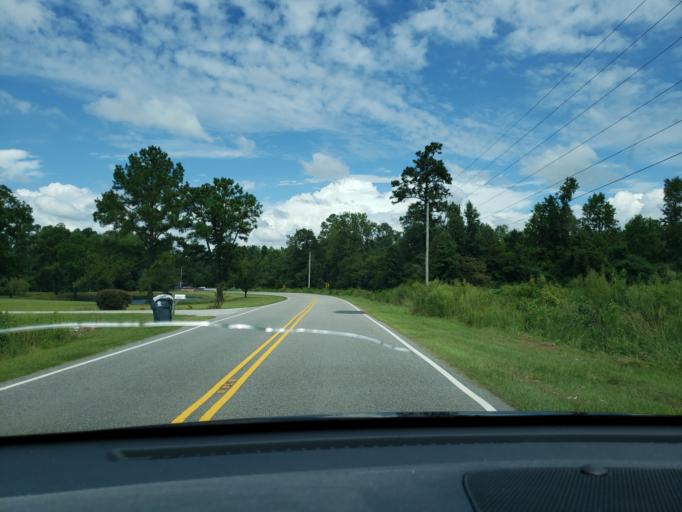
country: US
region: North Carolina
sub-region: Columbus County
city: Tabor City
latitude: 34.1753
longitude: -78.7853
